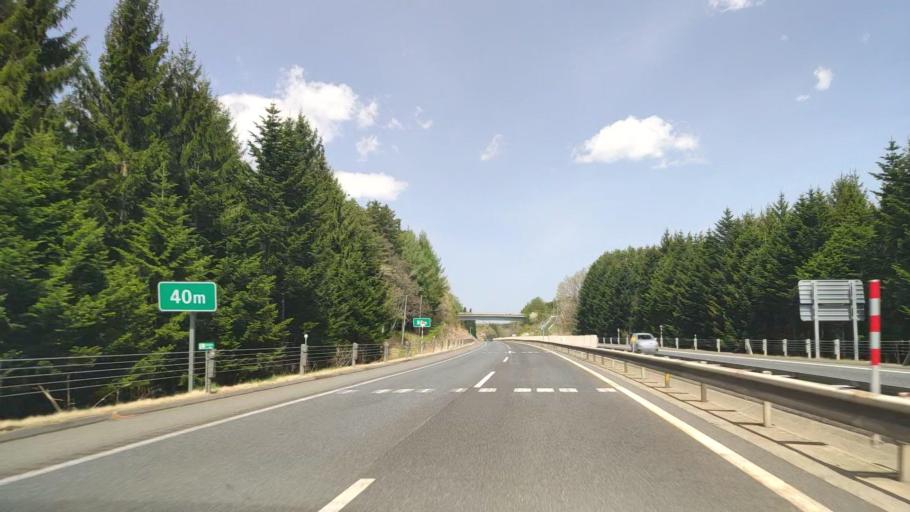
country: JP
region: Aomori
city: Hachinohe
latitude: 40.4135
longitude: 141.4431
